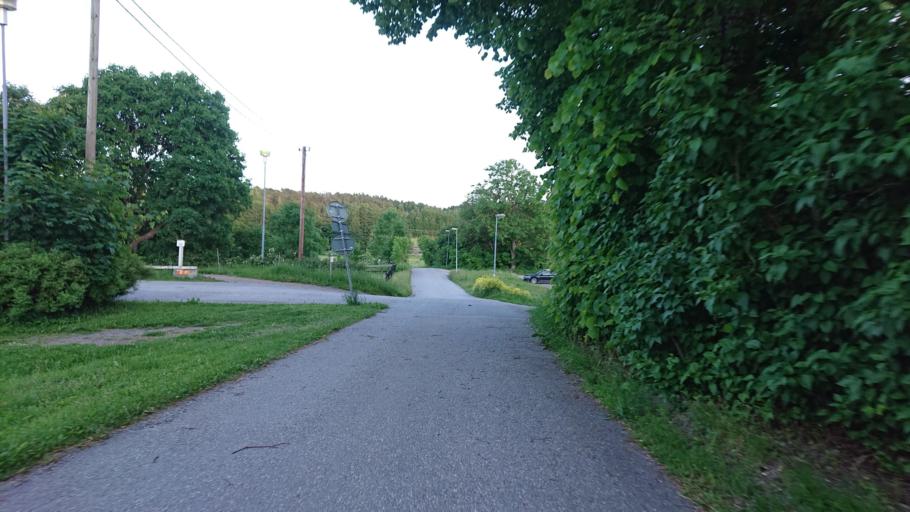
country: SE
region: Stockholm
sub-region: Osterakers Kommun
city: Akersberga
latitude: 59.5026
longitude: 18.3098
